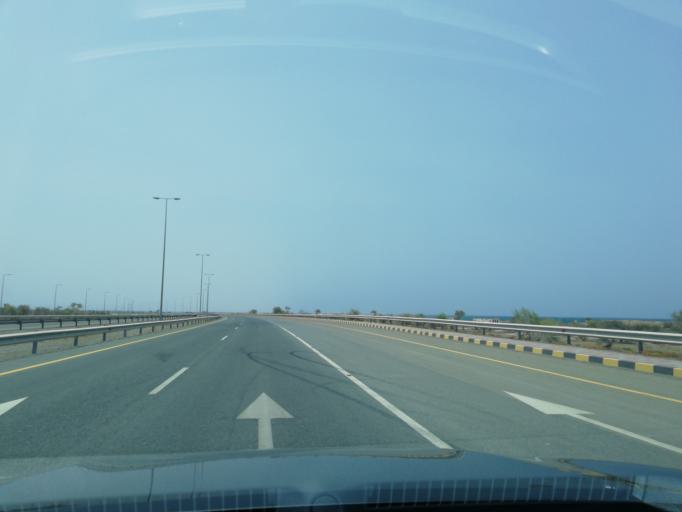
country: OM
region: Al Batinah
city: Shinas
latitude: 24.6564
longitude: 56.5126
